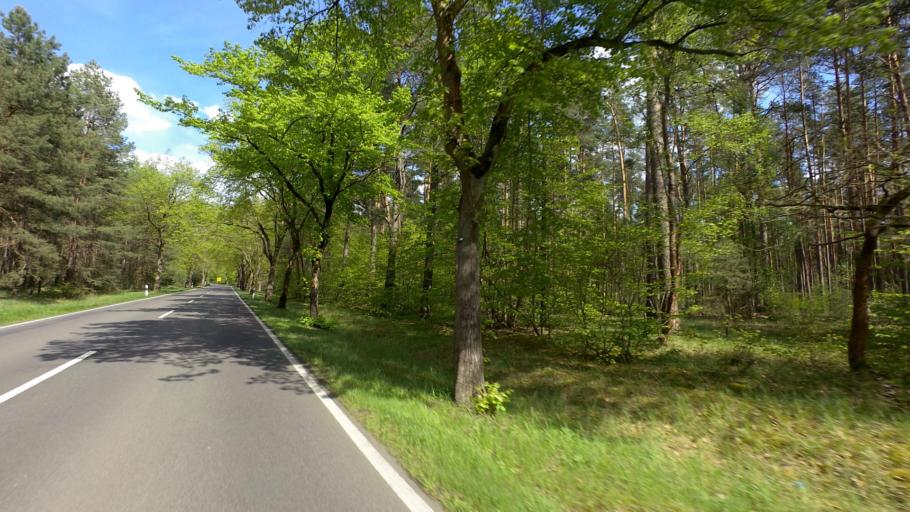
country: DE
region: Brandenburg
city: Milmersdorf
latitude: 53.0573
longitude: 13.6203
